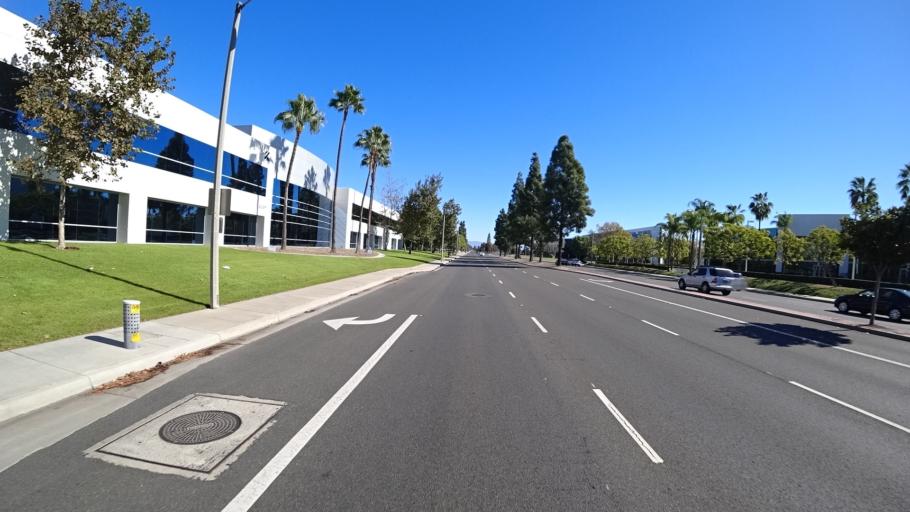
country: US
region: California
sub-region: Orange County
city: Cypress
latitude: 33.8030
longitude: -118.0237
